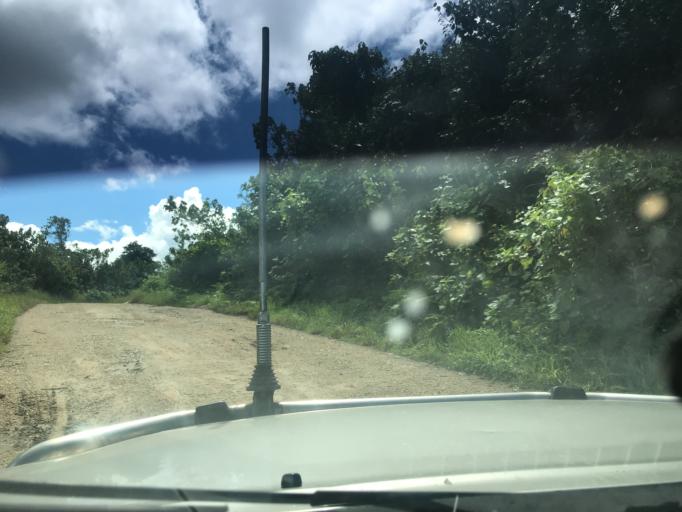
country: SB
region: Malaita
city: Auki
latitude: -8.7305
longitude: 160.9006
